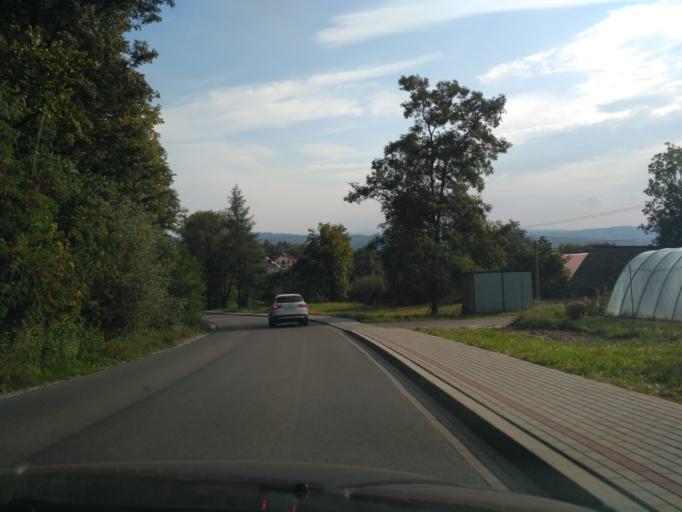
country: PL
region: Subcarpathian Voivodeship
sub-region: Powiat strzyzowski
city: Czudec
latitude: 49.9581
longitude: 21.8453
